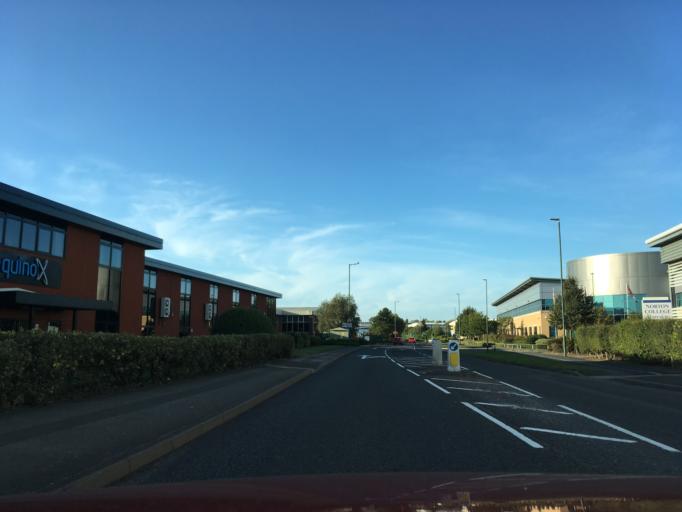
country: GB
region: England
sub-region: Worcestershire
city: Bredon
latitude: 52.0006
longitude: -2.1264
